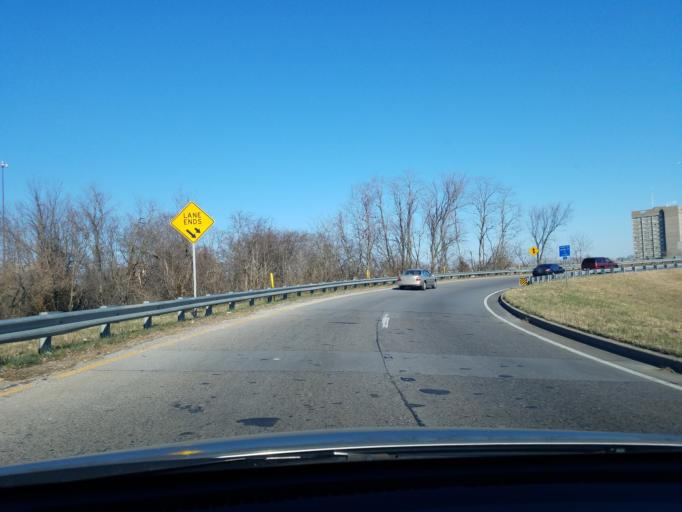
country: US
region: Indiana
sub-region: Floyd County
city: New Albany
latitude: 38.2846
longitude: -85.8302
